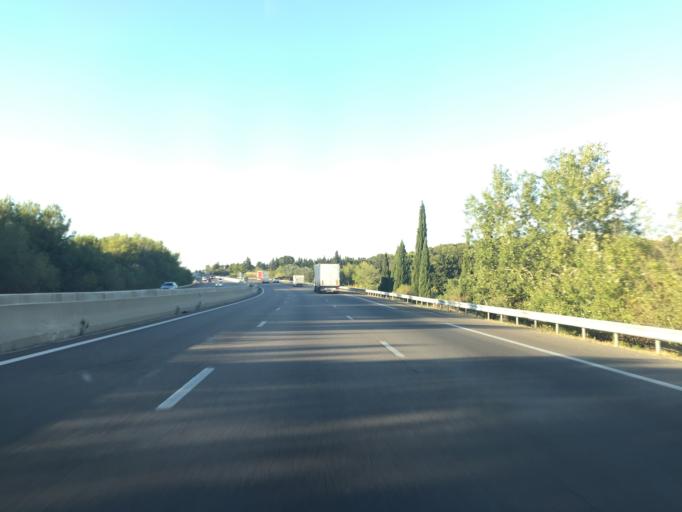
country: FR
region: Provence-Alpes-Cote d'Azur
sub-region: Departement du Vaucluse
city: Morieres-les-Avignon
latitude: 43.9128
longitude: 4.9143
